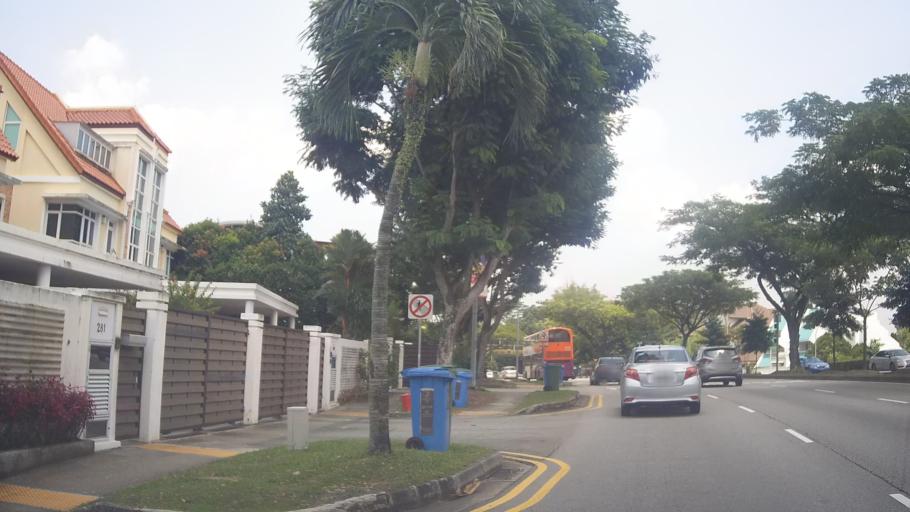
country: SG
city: Singapore
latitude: 1.3175
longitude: 103.7872
